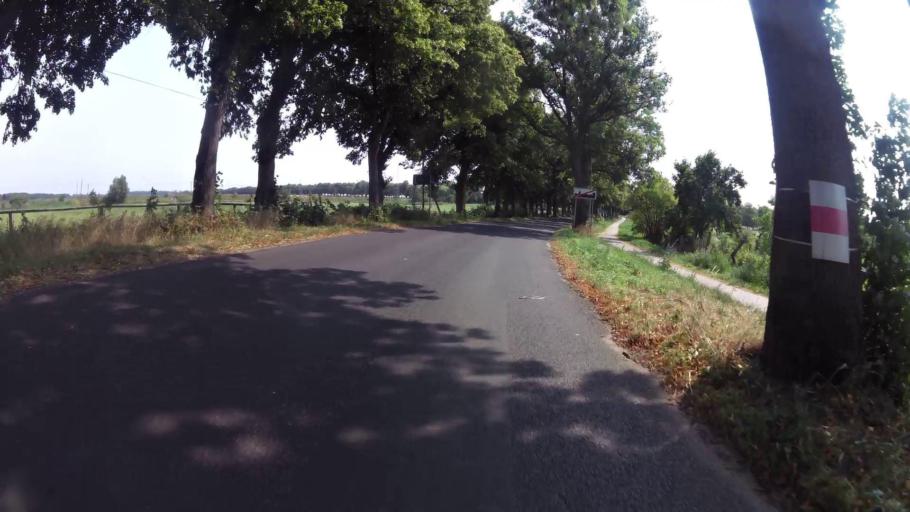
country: PL
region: West Pomeranian Voivodeship
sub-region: Powiat gryfinski
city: Mieszkowice
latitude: 52.8261
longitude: 14.4616
